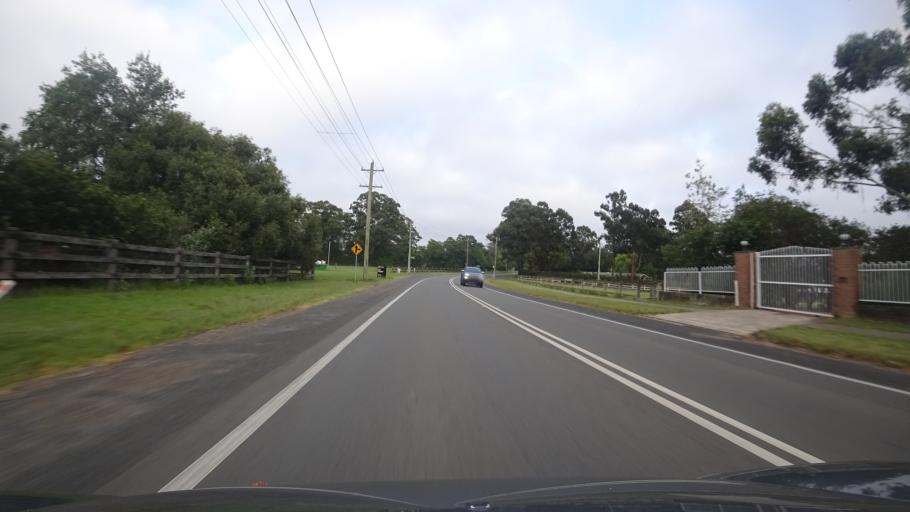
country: AU
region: New South Wales
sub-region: The Hills Shire
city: Beaumont Hills
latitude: -33.6712
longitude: 150.9550
